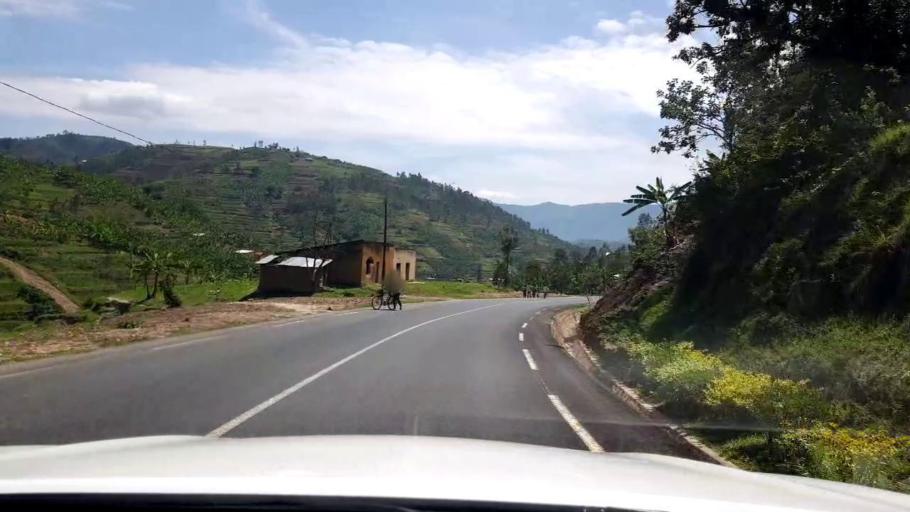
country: RW
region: Southern Province
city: Gitarama
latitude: -1.9194
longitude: 29.6412
